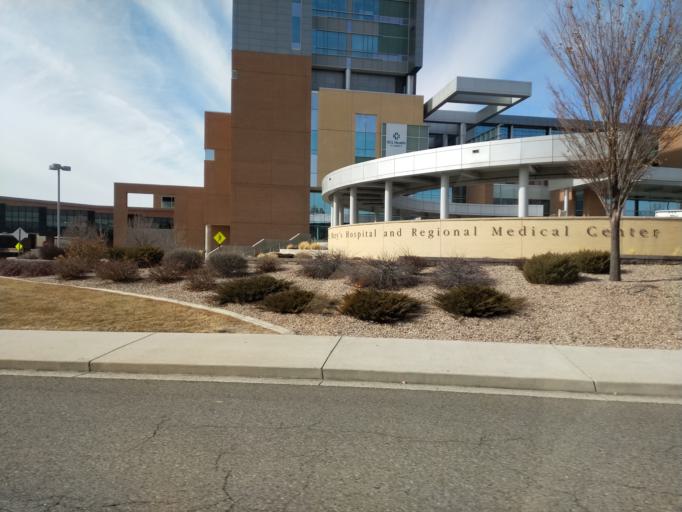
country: US
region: Colorado
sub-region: Mesa County
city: Grand Junction
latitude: 39.0905
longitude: -108.5615
